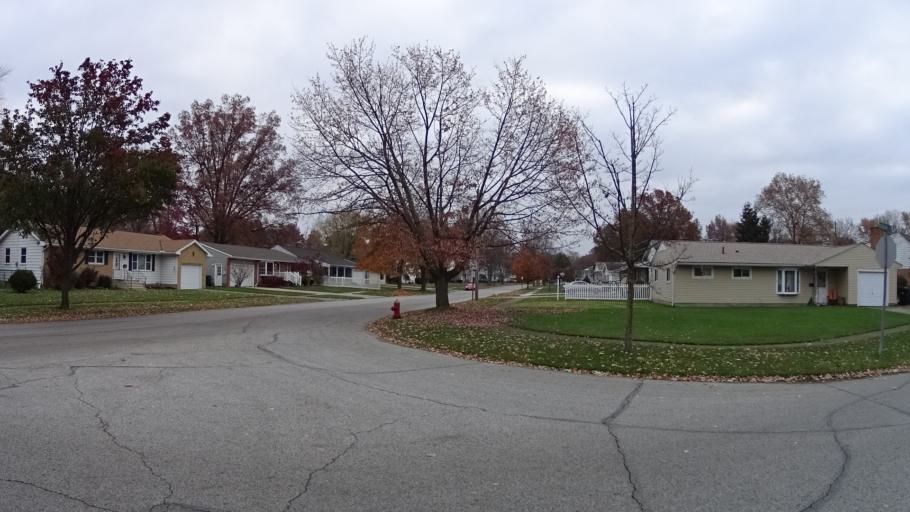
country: US
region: Ohio
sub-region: Lorain County
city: Elyria
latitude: 41.3544
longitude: -82.0982
